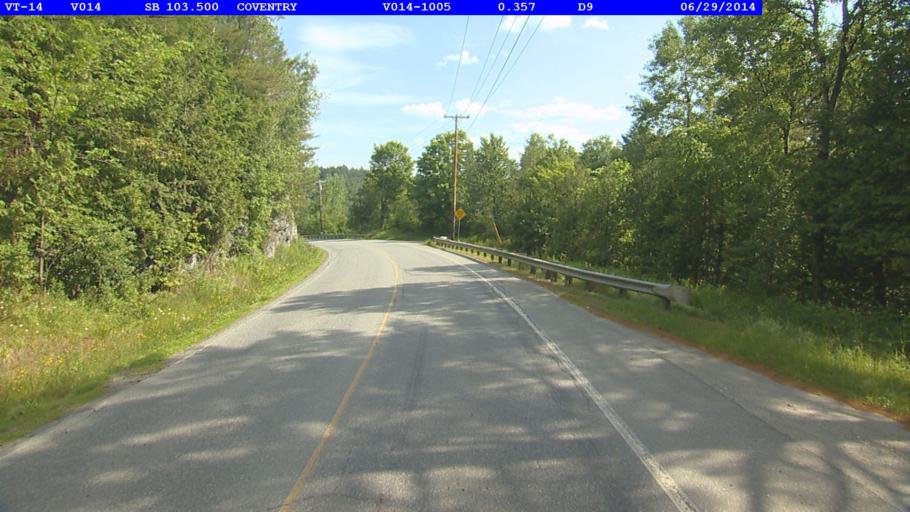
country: US
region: Vermont
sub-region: Orleans County
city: Newport
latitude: 44.8699
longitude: -72.2638
